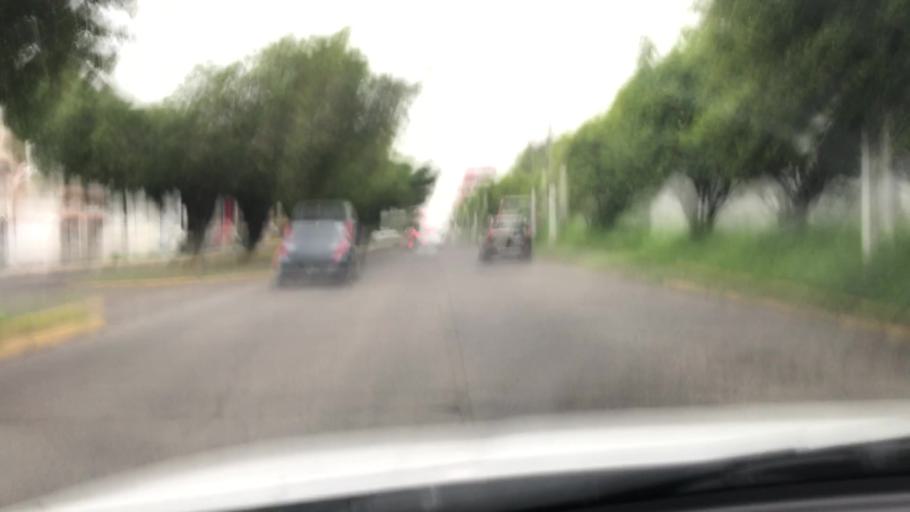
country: MX
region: Jalisco
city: Guadalajara
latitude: 20.6541
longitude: -103.4248
